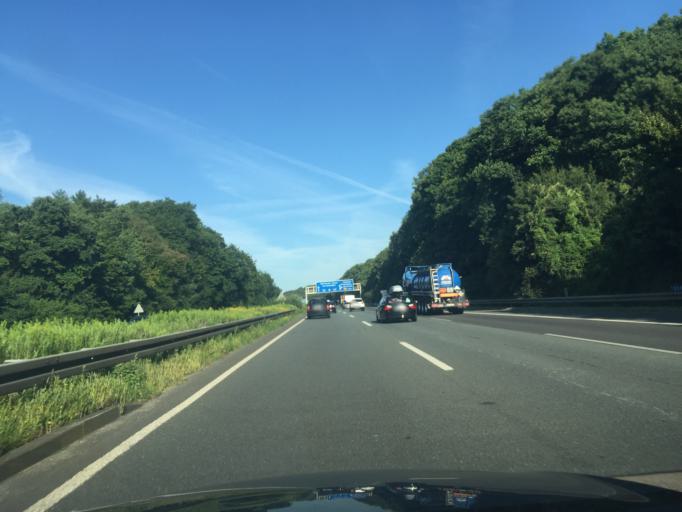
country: DE
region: North Rhine-Westphalia
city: Schwerte
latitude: 51.4408
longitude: 7.5113
